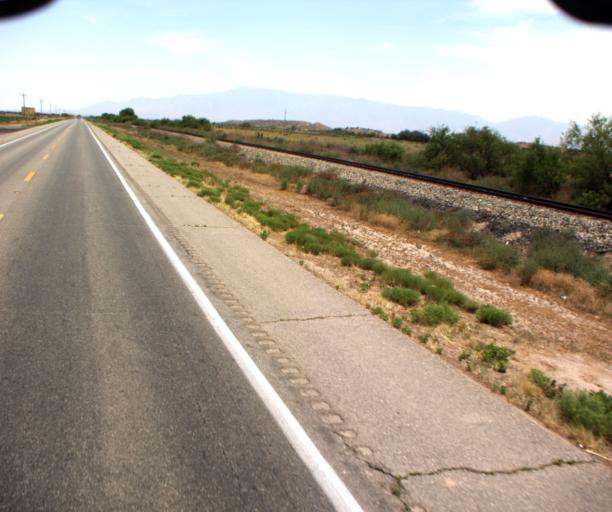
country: US
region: Arizona
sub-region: Graham County
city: Pima
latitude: 33.0117
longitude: -109.9498
